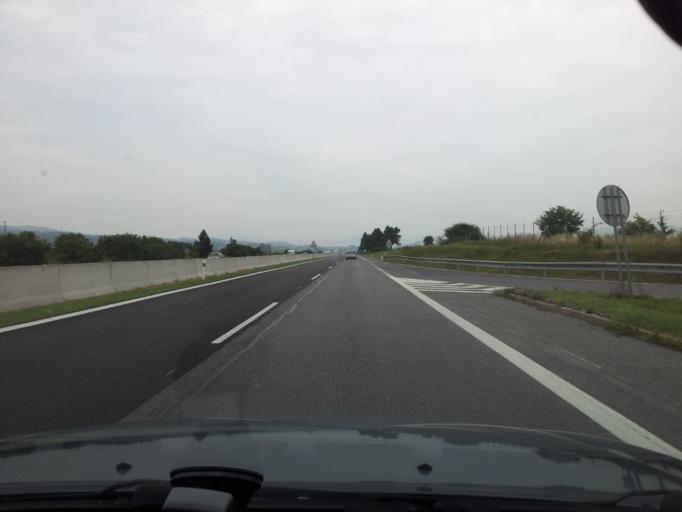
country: SK
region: Banskobystricky
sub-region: Okres Banska Bystrica
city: Zvolen
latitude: 48.6304
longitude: 19.1193
